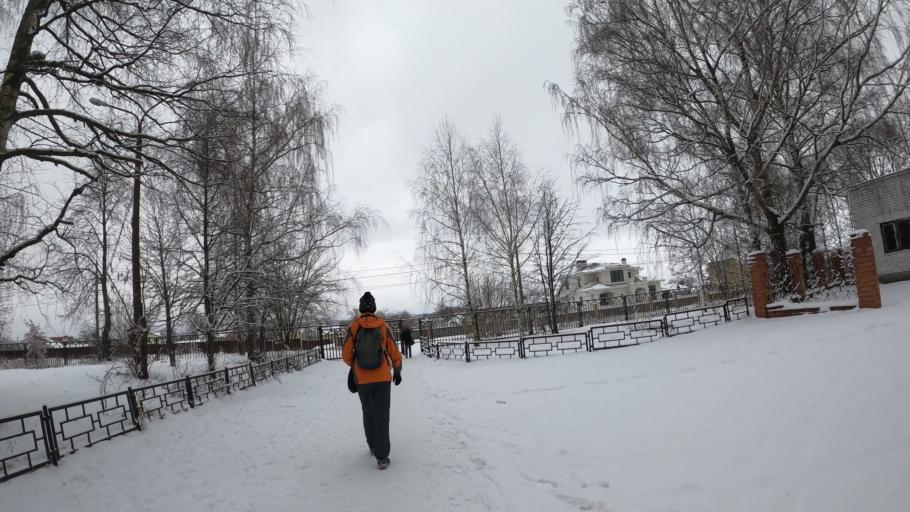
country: RU
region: Jaroslavl
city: Pereslavl'-Zalesskiy
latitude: 56.7466
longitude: 38.8643
